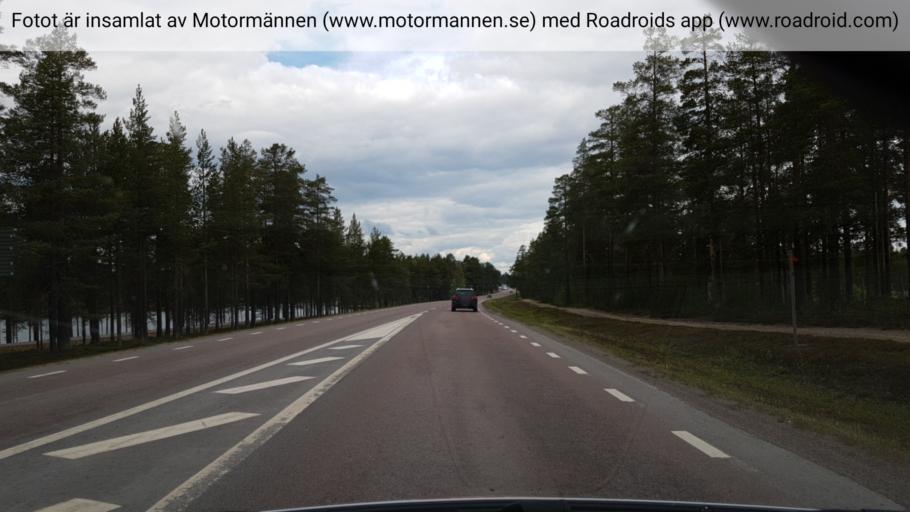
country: SE
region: Norrbotten
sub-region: Arvidsjaurs Kommun
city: Arvidsjaur
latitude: 65.5811
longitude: 19.2071
